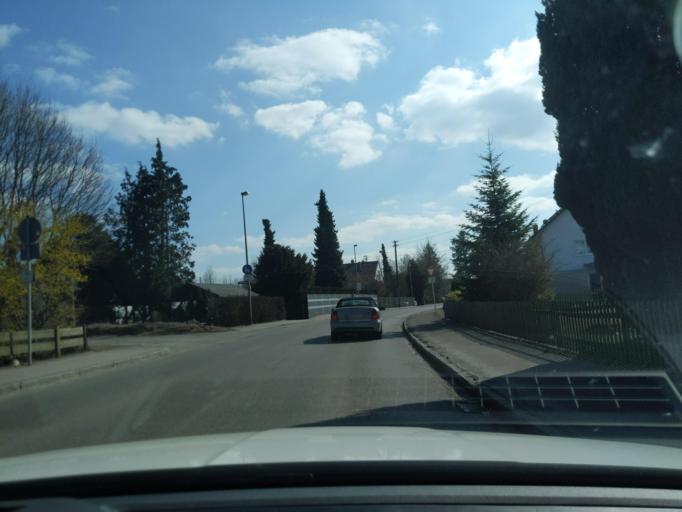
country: DE
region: Bavaria
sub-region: Swabia
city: Vohringen
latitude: 48.3190
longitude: 10.1017
